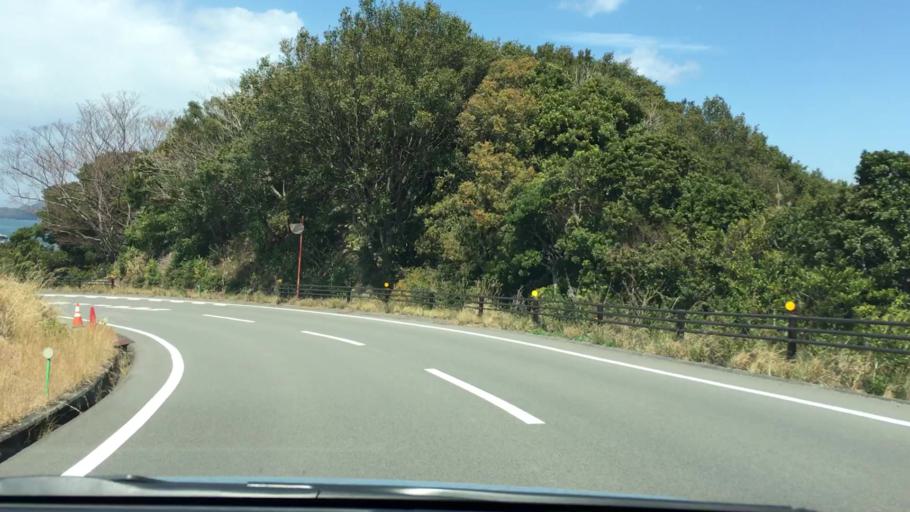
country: JP
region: Mie
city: Toba
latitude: 34.4483
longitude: 136.9109
